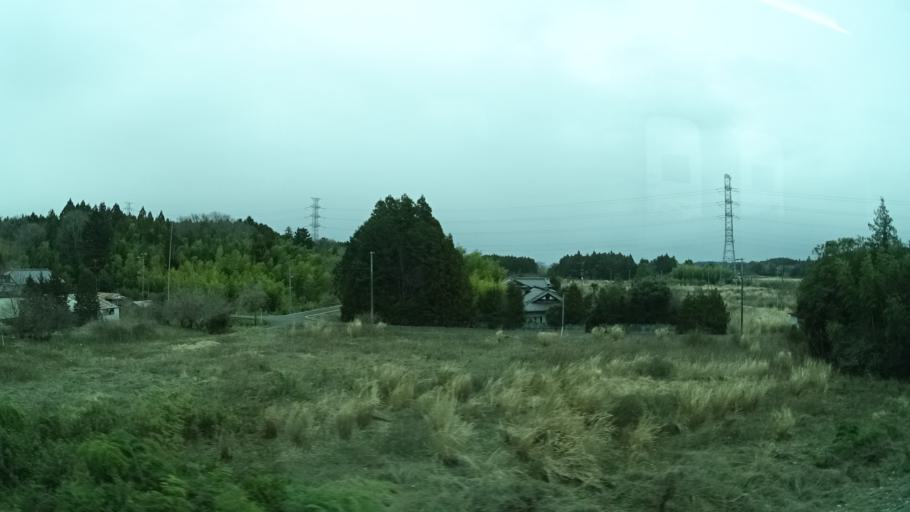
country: JP
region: Fukushima
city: Namie
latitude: 37.3890
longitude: 140.9890
